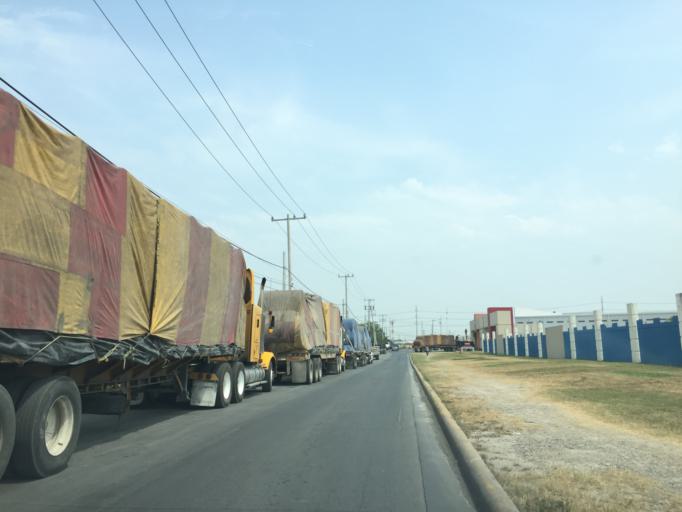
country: MX
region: Nuevo Leon
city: Apodaca
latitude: 25.7627
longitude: -100.1969
